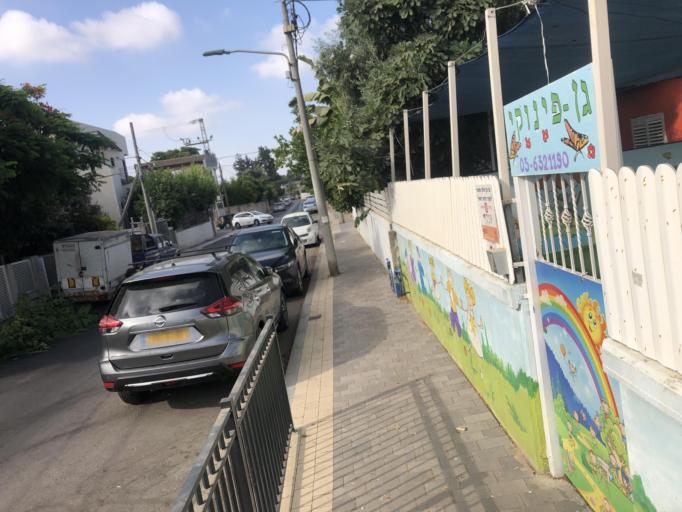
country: IL
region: Central District
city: Yehud
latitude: 32.0331
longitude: 34.8832
